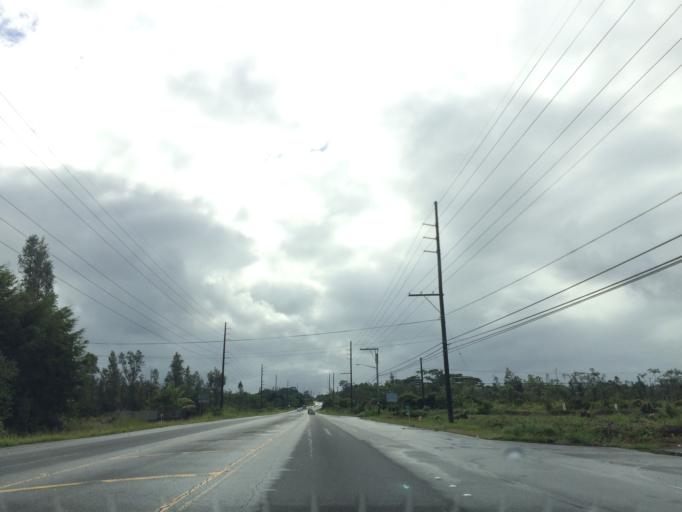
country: US
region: Hawaii
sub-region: Hawaii County
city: Ainaloa
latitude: 19.5542
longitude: -154.9866
